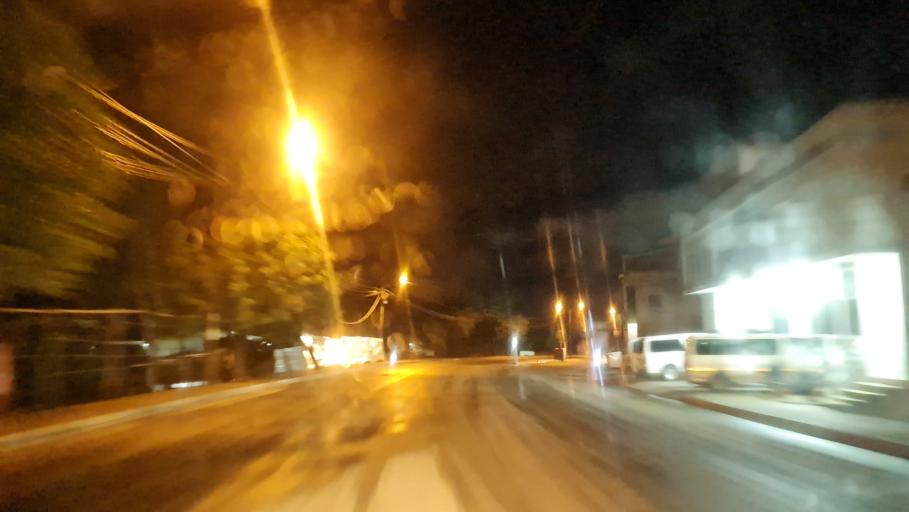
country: MZ
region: Nampula
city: Nampula
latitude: -15.1143
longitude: 39.2821
